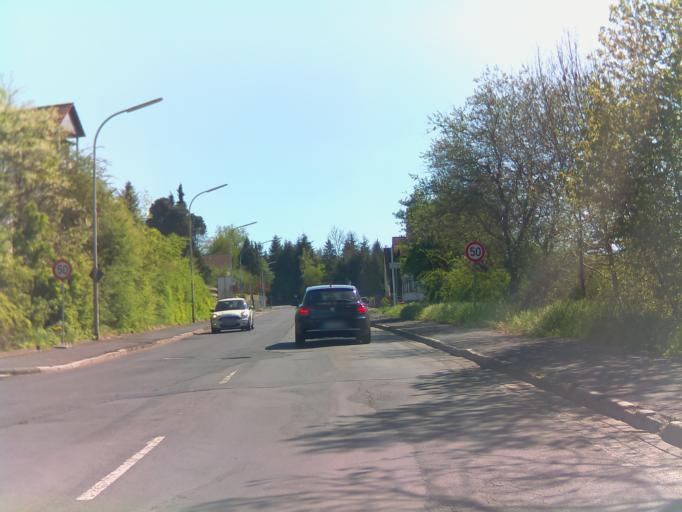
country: DE
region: Hesse
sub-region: Regierungsbezirk Giessen
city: Lauterbach
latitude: 50.6181
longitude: 9.3896
